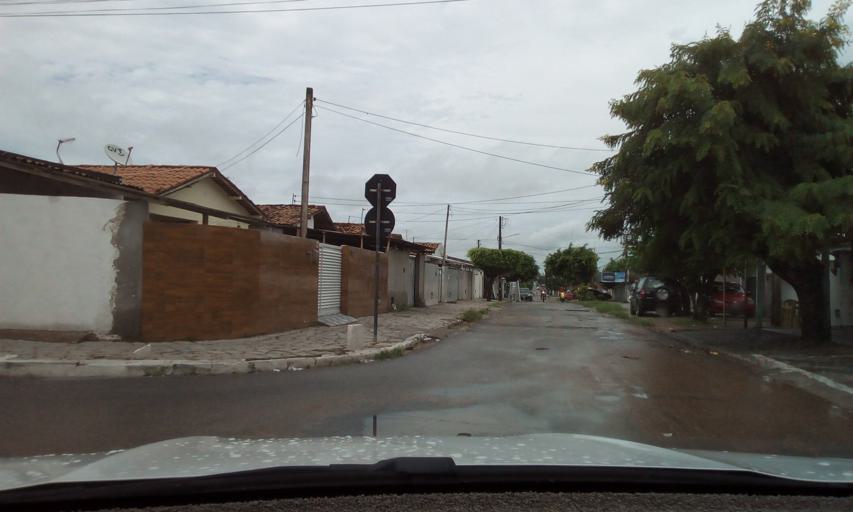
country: BR
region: Paraiba
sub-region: Joao Pessoa
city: Joao Pessoa
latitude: -7.1667
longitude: -34.8366
